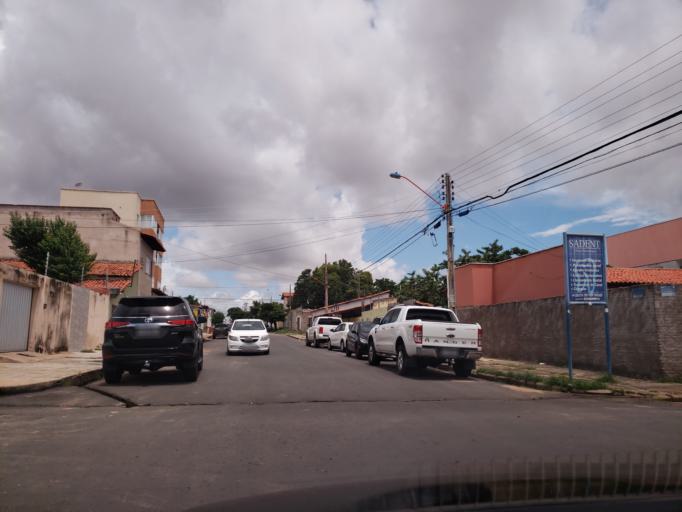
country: BR
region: Piaui
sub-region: Teresina
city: Teresina
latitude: -5.1089
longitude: -42.8101
